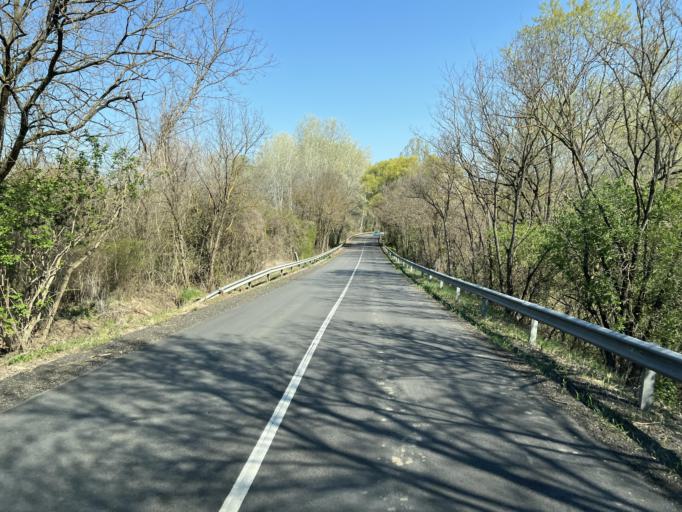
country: HU
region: Pest
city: Orbottyan
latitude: 47.7289
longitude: 19.2694
